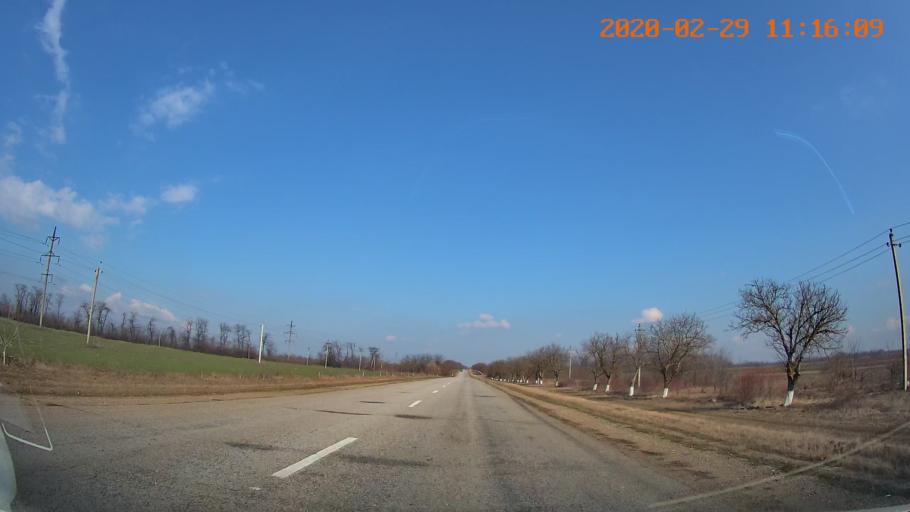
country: MD
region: Telenesti
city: Dubasari
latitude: 47.3047
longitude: 29.1670
